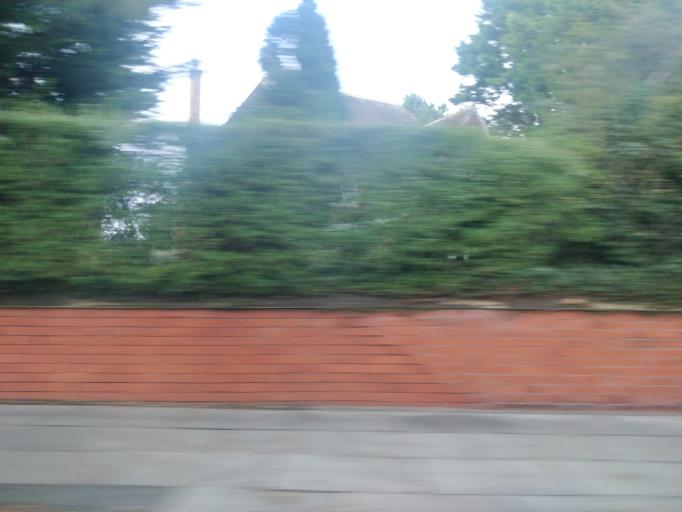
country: GB
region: England
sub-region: Sefton
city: Southport
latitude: 53.6602
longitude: -2.9806
